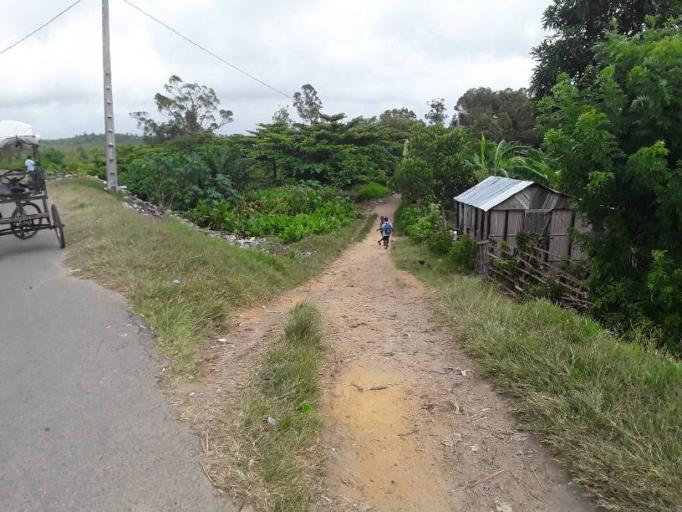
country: MG
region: Atsinanana
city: Andovoranto
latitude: -19.3361
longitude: 48.9728
